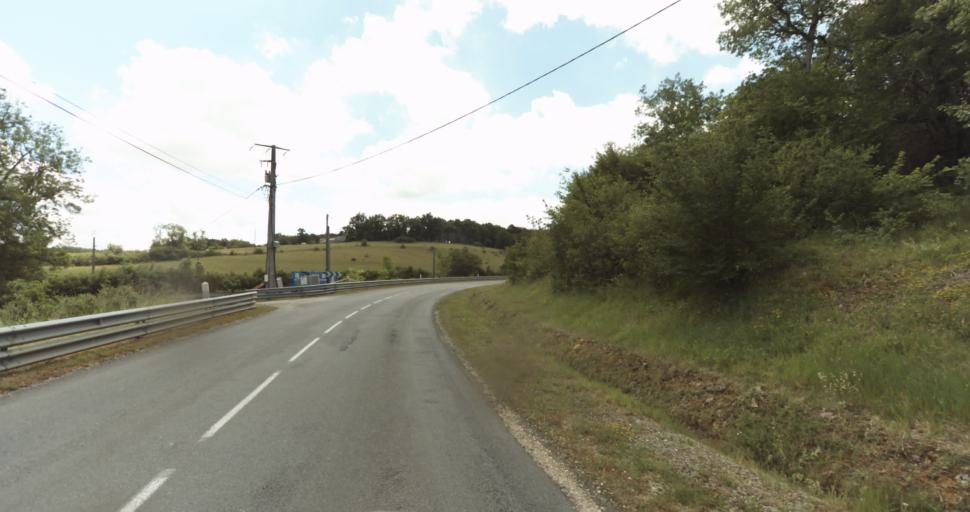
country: FR
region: Aquitaine
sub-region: Departement de la Dordogne
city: Beaumont-du-Perigord
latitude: 44.7469
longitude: 0.7611
